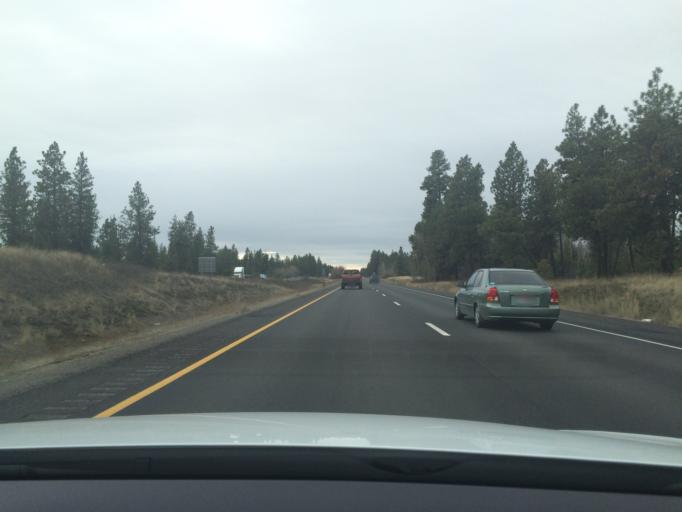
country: US
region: Washington
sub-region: Spokane County
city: Medical Lake
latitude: 47.4932
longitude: -117.7075
